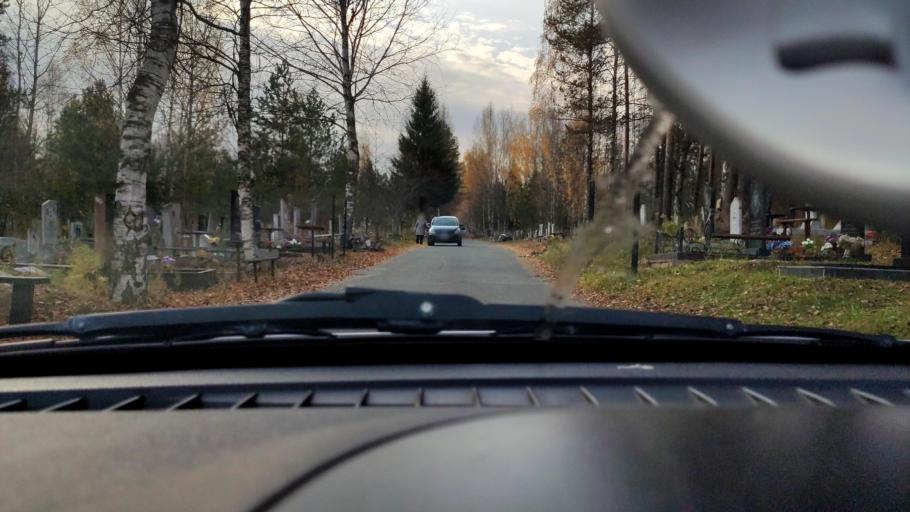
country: RU
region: Perm
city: Kondratovo
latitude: 58.0671
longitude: 56.1336
